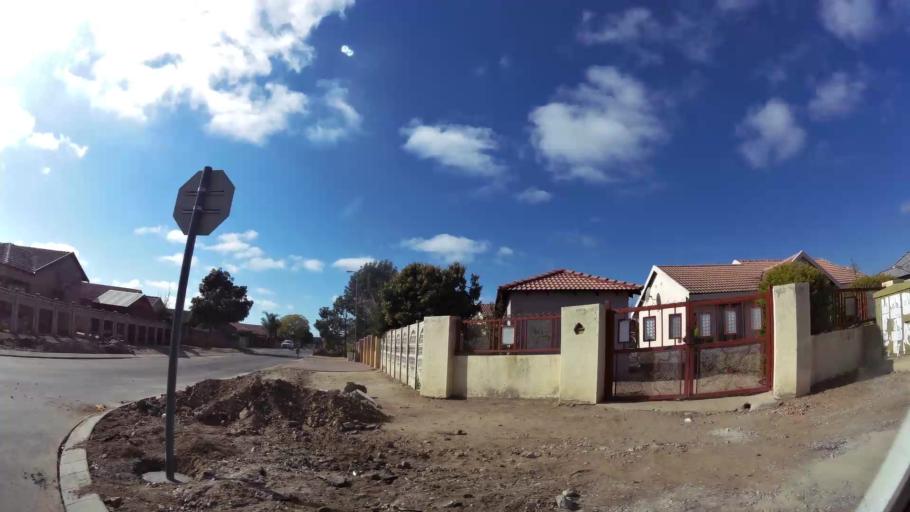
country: ZA
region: Limpopo
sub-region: Capricorn District Municipality
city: Polokwane
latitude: -23.8553
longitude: 29.3727
